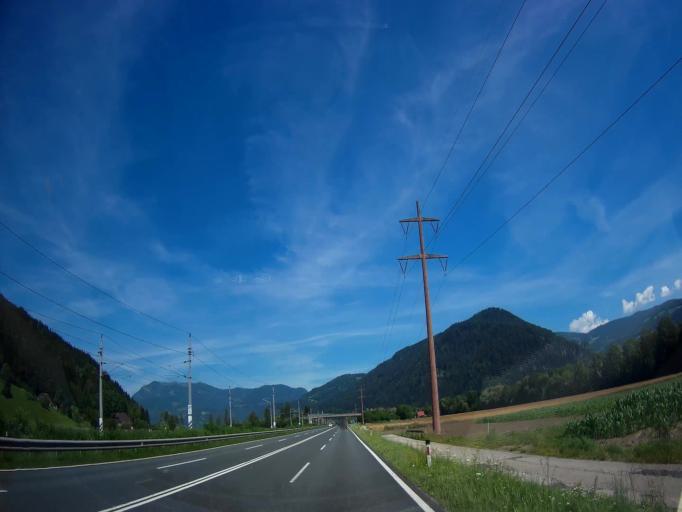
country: AT
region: Carinthia
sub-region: Politischer Bezirk Sankt Veit an der Glan
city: Micheldorf
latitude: 46.9362
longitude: 14.4256
